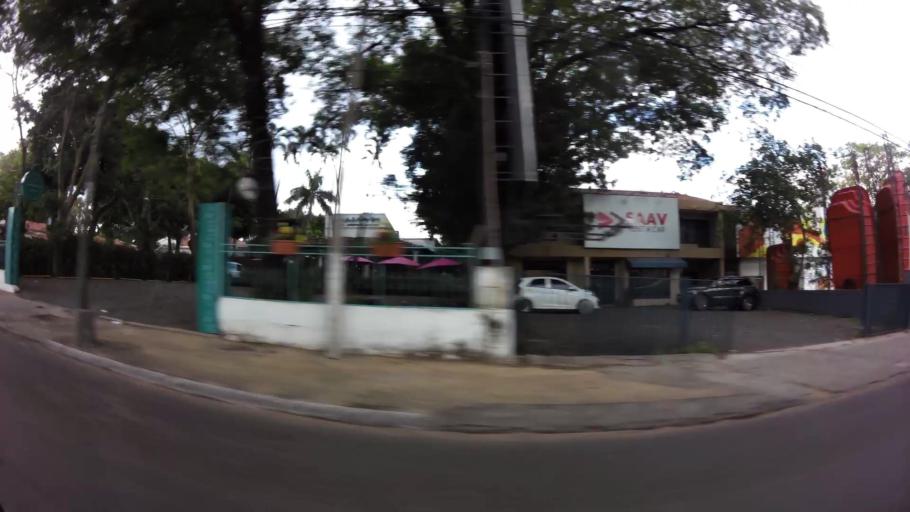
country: PY
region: Asuncion
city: Asuncion
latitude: -25.2908
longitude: -57.5940
